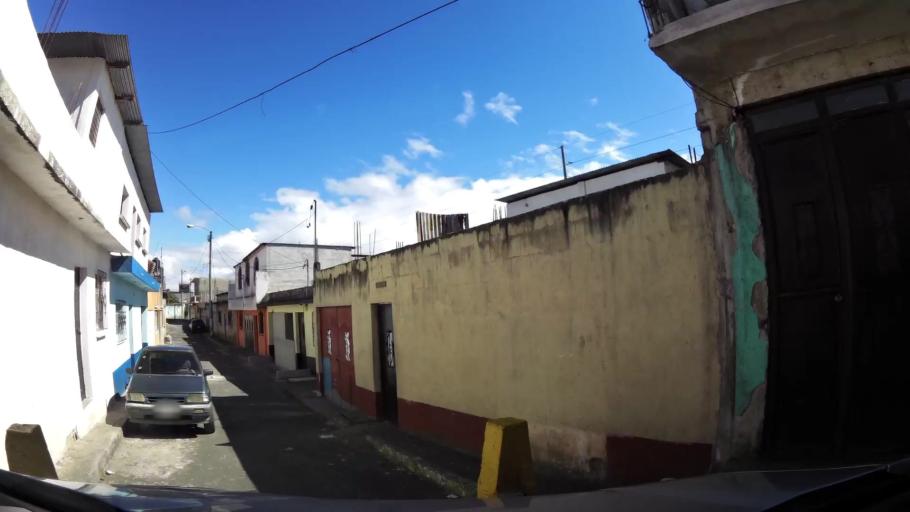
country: GT
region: Guatemala
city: Guatemala City
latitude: 14.6077
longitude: -90.5302
